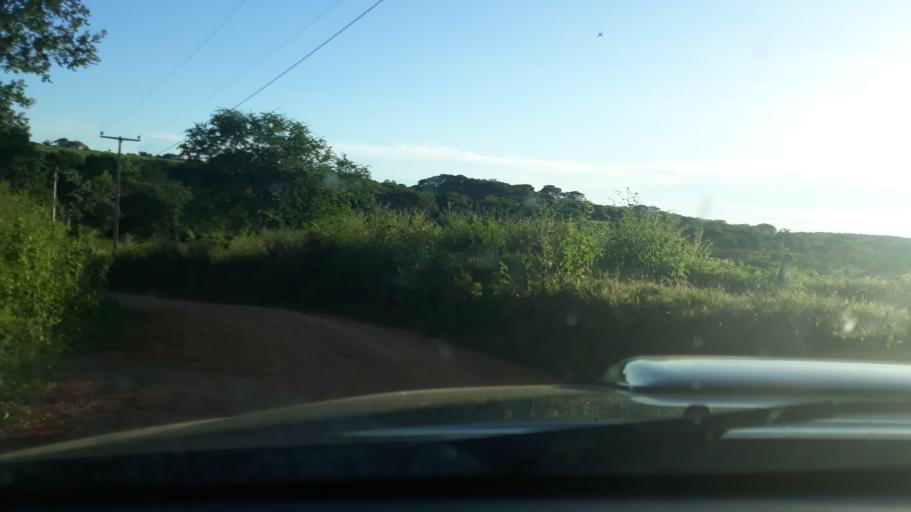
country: BR
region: Bahia
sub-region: Riacho De Santana
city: Riacho de Santana
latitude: -13.8443
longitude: -42.7415
